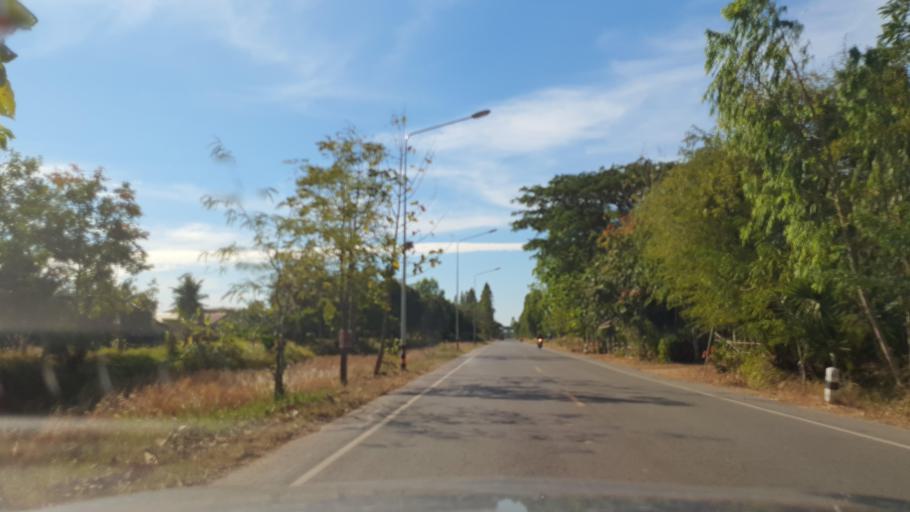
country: TH
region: Kalasin
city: Khao Wong
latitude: 16.6500
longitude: 104.1523
